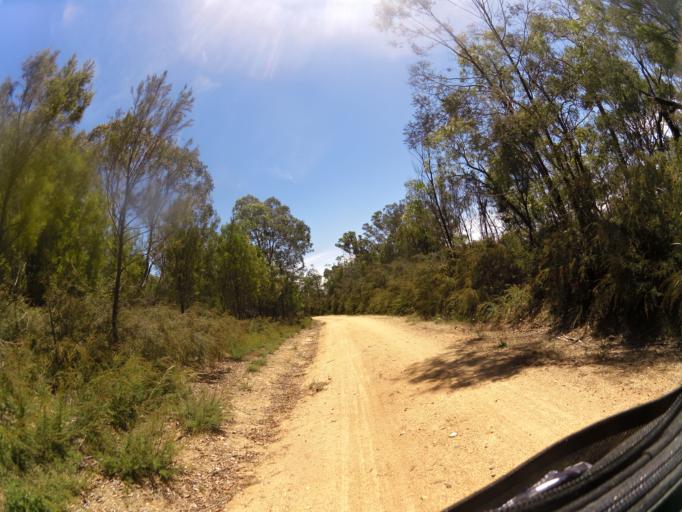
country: AU
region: Victoria
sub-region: East Gippsland
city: Lakes Entrance
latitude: -37.7307
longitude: 147.8593
